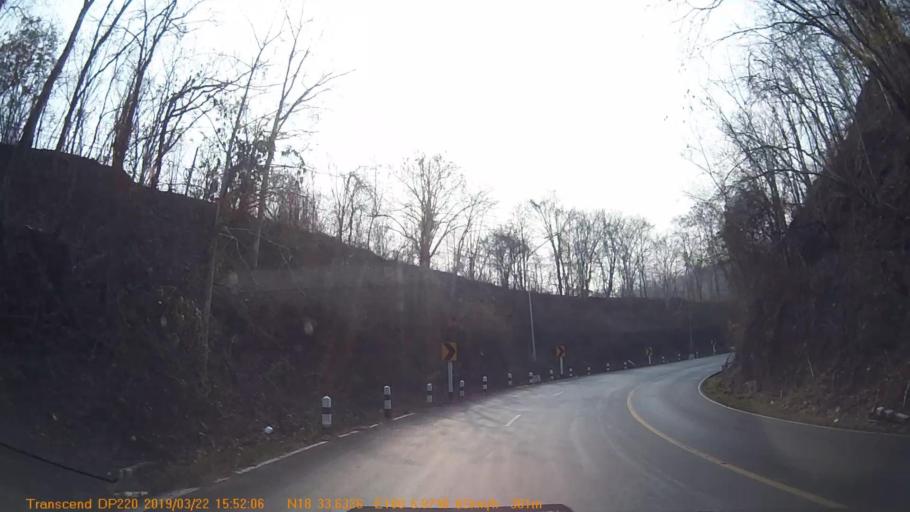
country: TH
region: Phrae
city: Song
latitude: 18.5605
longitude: 100.0993
